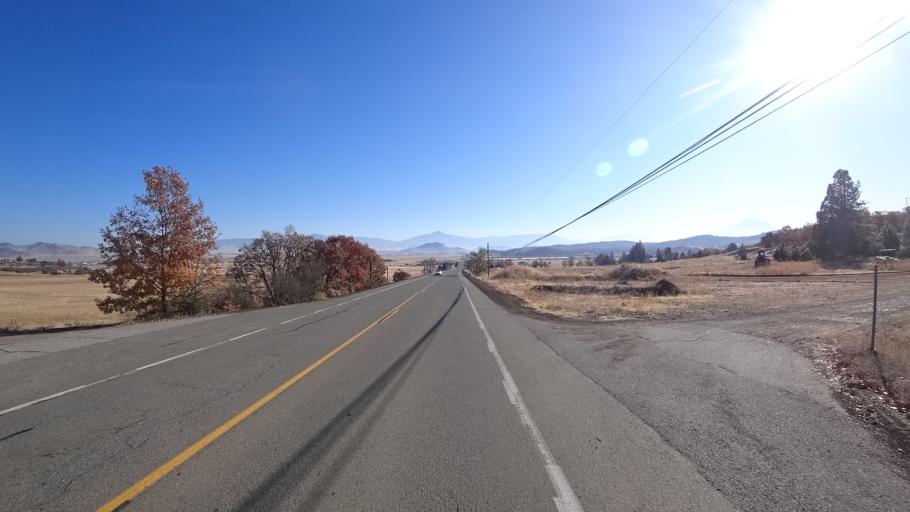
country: US
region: California
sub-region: Siskiyou County
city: Yreka
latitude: 41.7120
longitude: -122.6133
